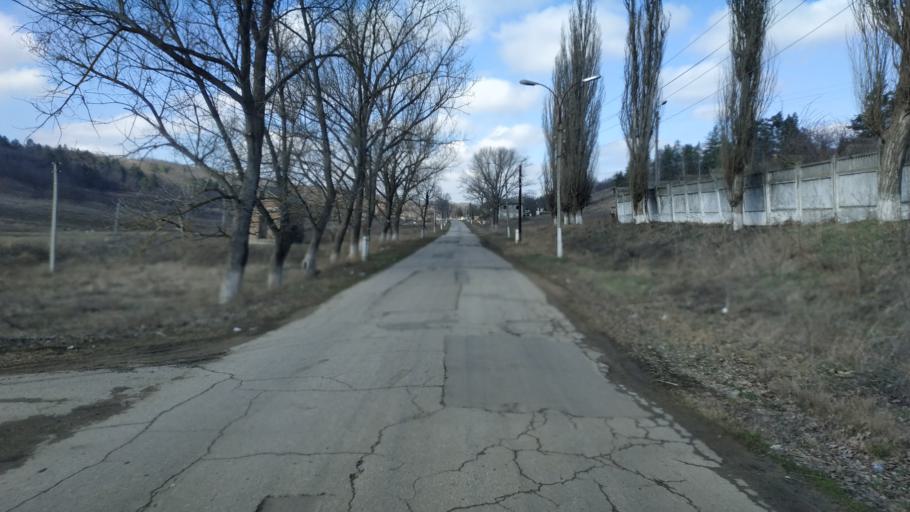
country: MD
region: Hincesti
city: Hincesti
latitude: 46.8703
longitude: 28.6371
